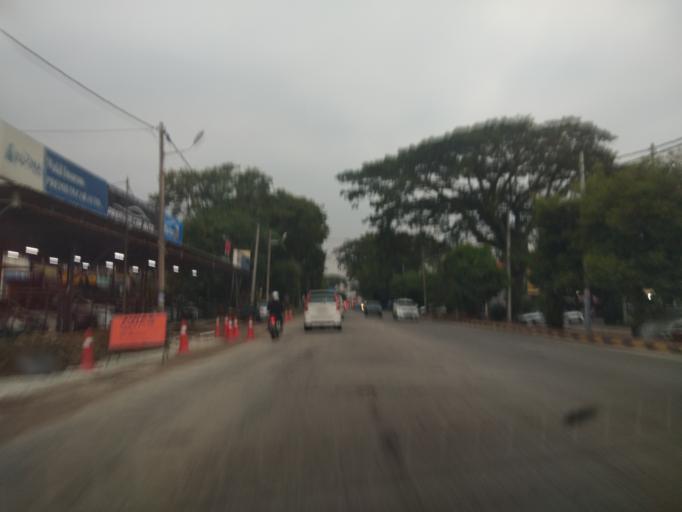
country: MY
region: Penang
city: Permatang Kuching
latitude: 5.4387
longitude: 100.3811
